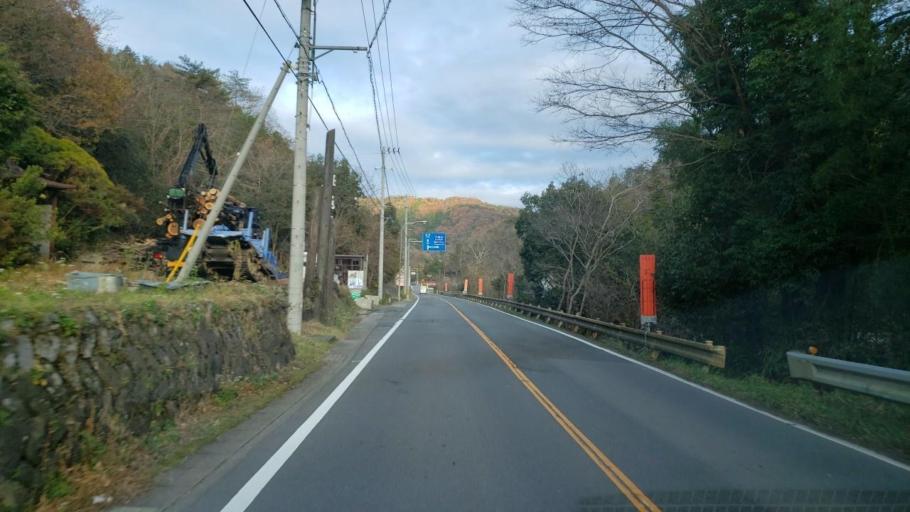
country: JP
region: Tokushima
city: Wakimachi
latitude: 34.1701
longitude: 134.0927
